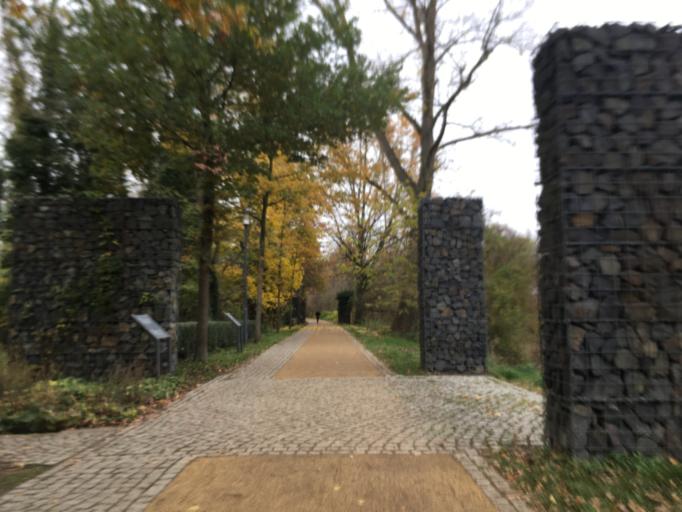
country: DE
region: Brandenburg
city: Frankfurt (Oder)
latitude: 52.3365
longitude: 14.5592
